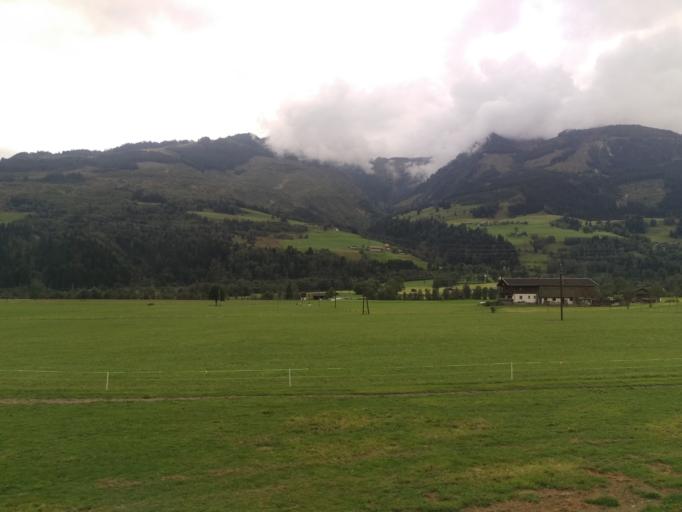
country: AT
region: Salzburg
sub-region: Politischer Bezirk Zell am See
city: Piesendorf
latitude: 47.2860
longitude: 12.6994
